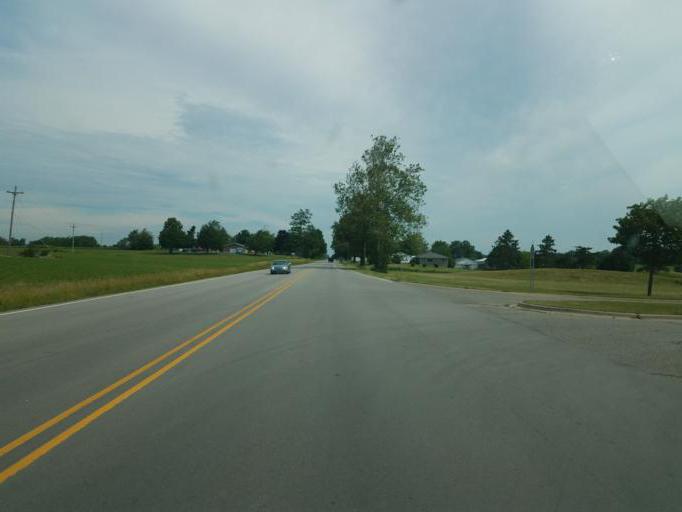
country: US
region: Michigan
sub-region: Eaton County
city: Charlotte
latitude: 42.5874
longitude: -84.8361
